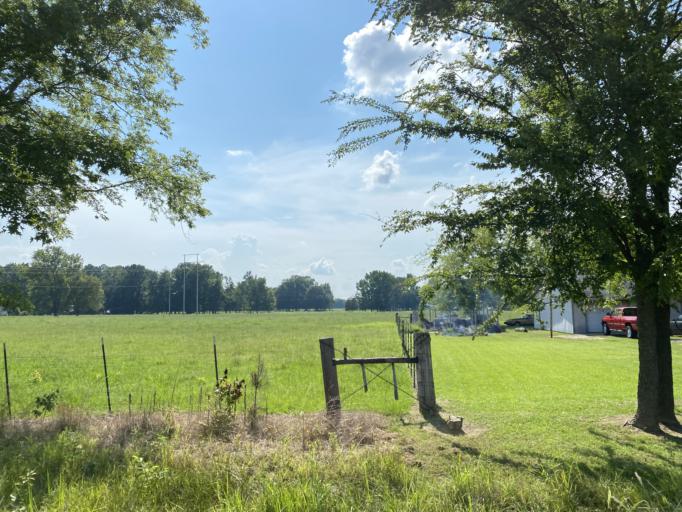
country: US
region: Alabama
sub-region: Lawrence County
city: Town Creek
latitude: 34.6614
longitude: -87.4057
